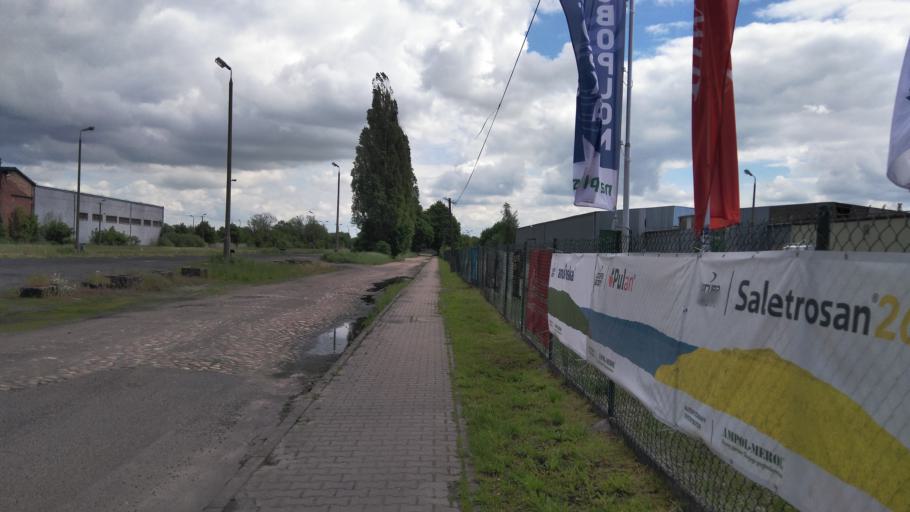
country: PL
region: Kujawsko-Pomorskie
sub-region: Powiat grudziadzki
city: Gruta
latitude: 53.4375
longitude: 18.9435
